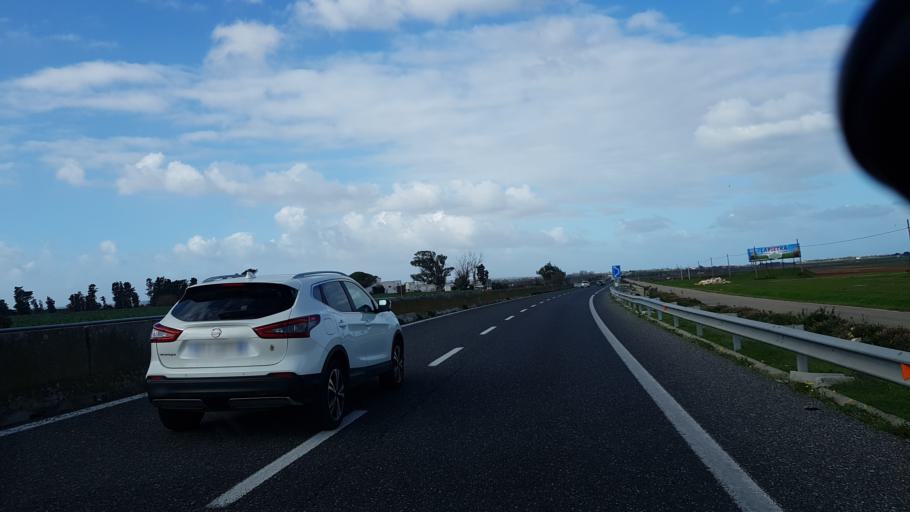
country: IT
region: Apulia
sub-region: Provincia di Brindisi
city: Brindisi
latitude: 40.6710
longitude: 17.8563
